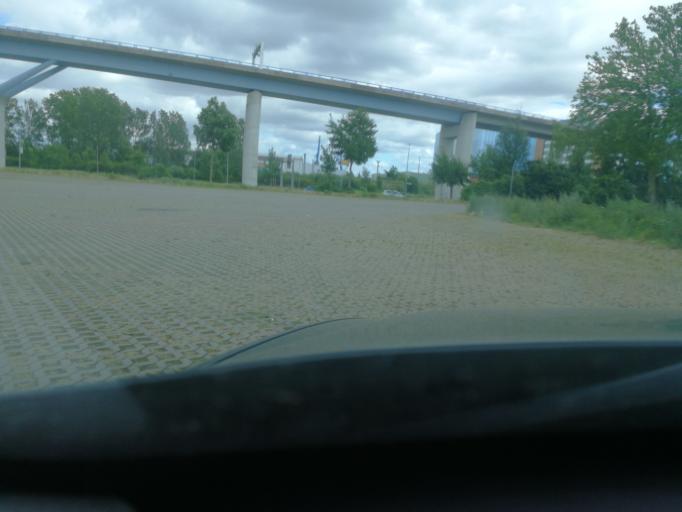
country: DE
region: Mecklenburg-Vorpommern
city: Stralsund
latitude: 54.3049
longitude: 13.1026
